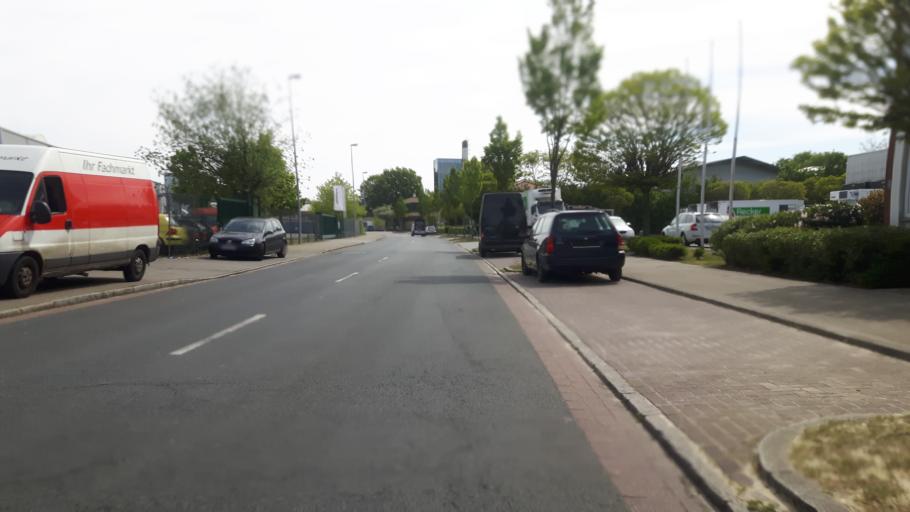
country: DE
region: Lower Saxony
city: Stuhr
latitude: 53.0587
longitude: 8.7742
